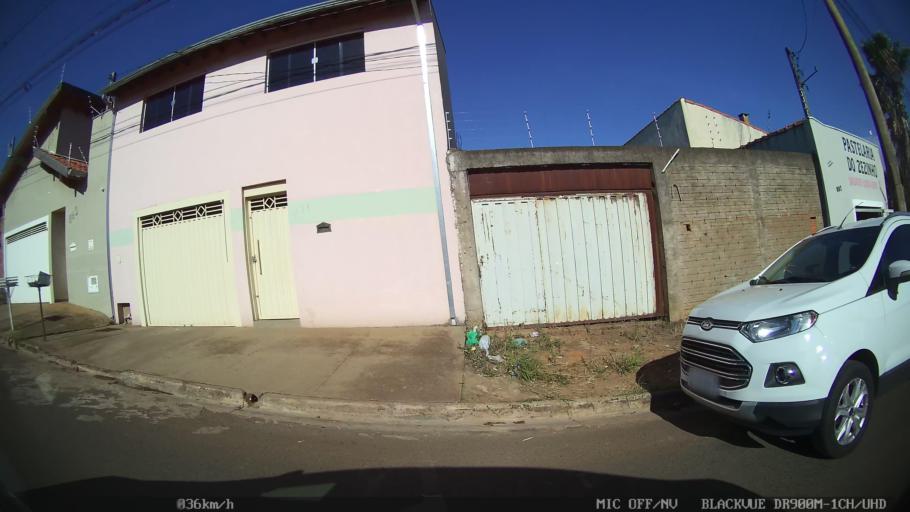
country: BR
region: Sao Paulo
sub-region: Franca
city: Franca
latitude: -20.4806
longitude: -47.4200
